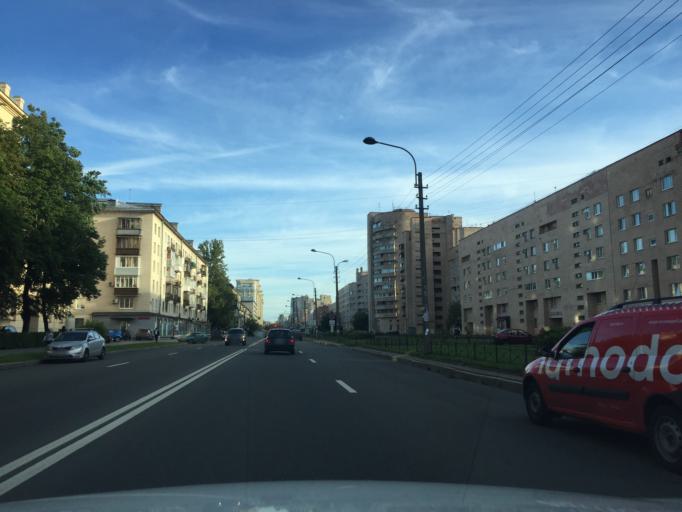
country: RU
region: St.-Petersburg
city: Kupchino
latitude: 59.8634
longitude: 30.3140
